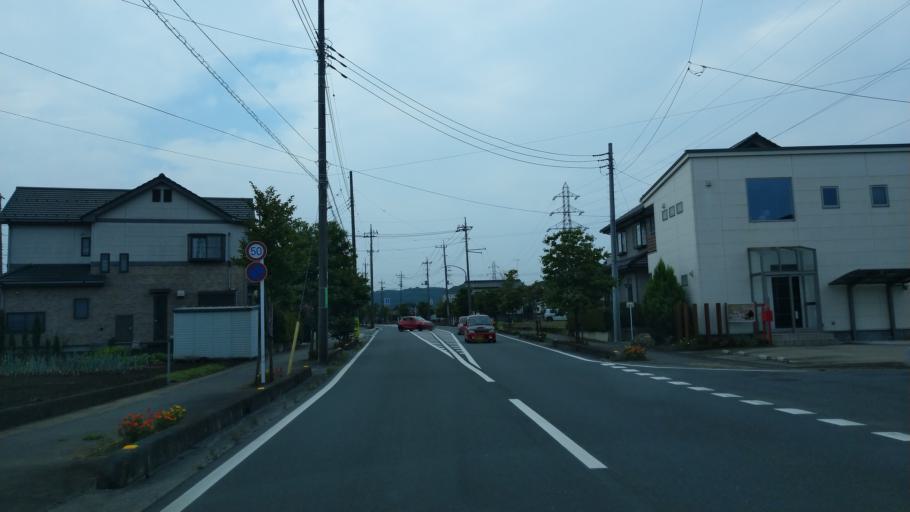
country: JP
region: Saitama
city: Morohongo
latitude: 35.8981
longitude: 139.3318
